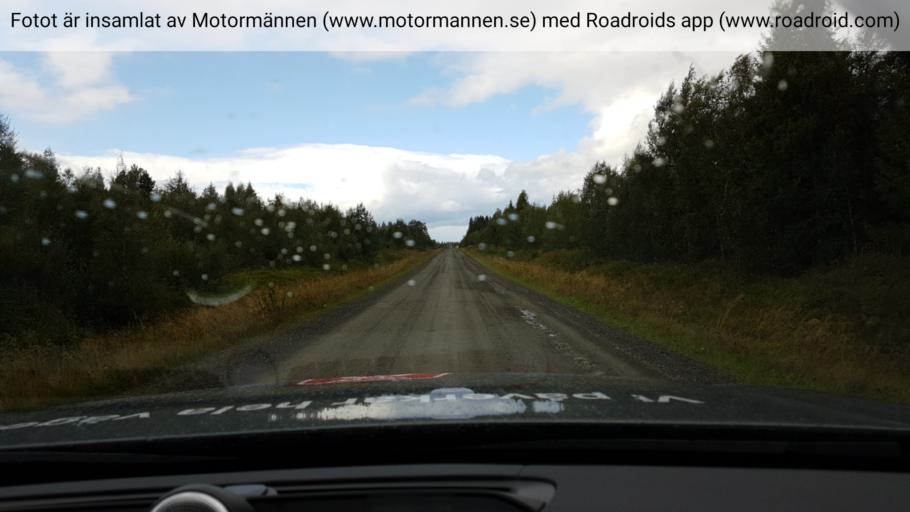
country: SE
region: Jaemtland
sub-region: OEstersunds Kommun
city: Lit
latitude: 63.6764
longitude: 14.8706
